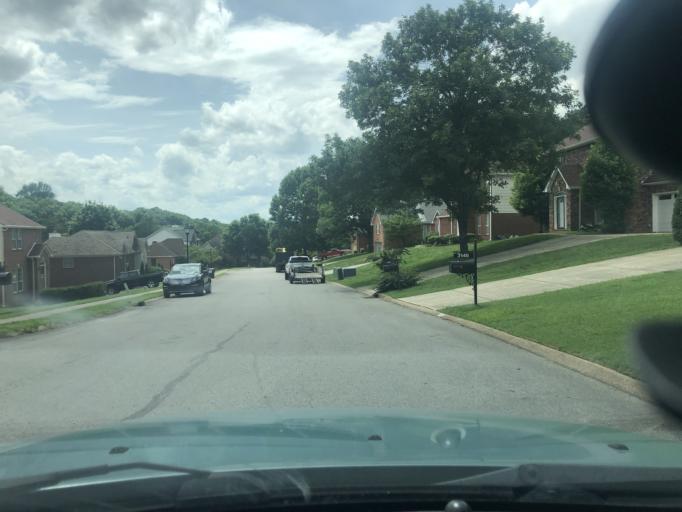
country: US
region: Tennessee
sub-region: Davidson County
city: Lakewood
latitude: 36.1329
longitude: -86.6321
